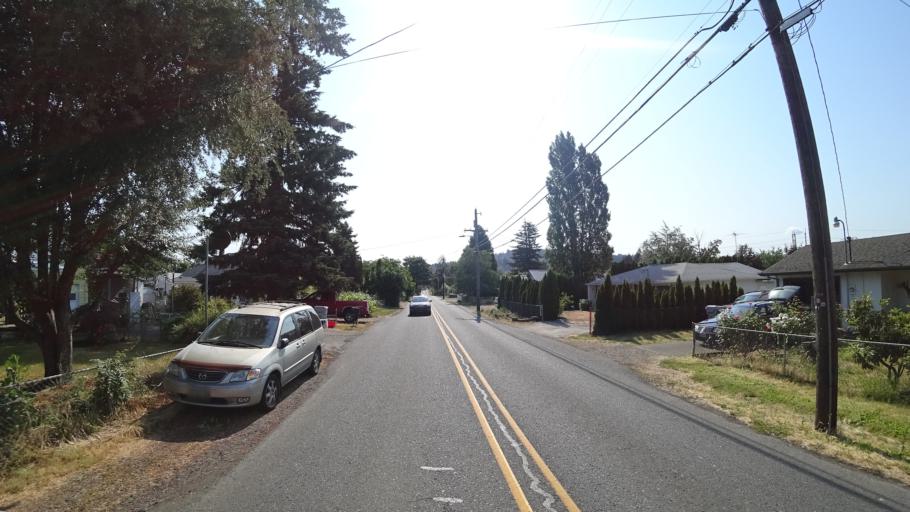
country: US
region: Oregon
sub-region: Multnomah County
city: Lents
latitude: 45.4611
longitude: -122.5871
